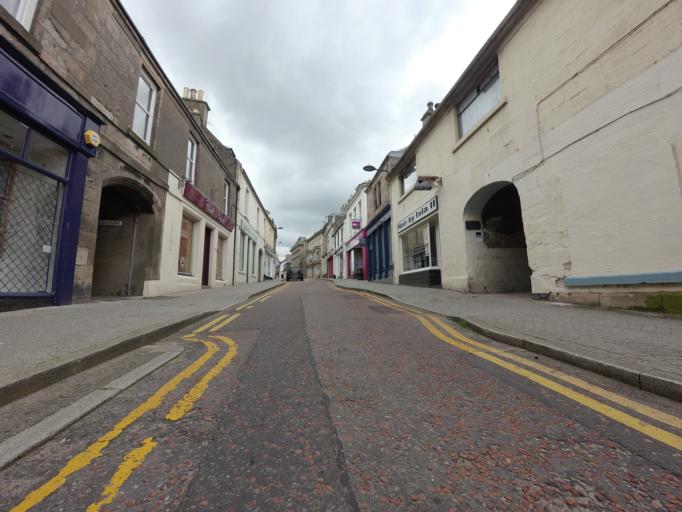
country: GB
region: Scotland
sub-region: Highland
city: Nairn
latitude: 57.5859
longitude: -3.8662
